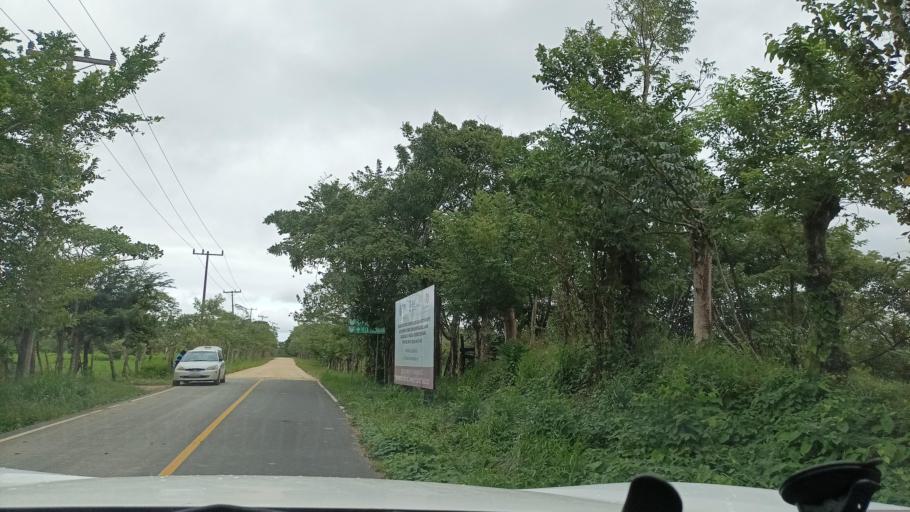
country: MX
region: Veracruz
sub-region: Moloacan
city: Cuichapa
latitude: 17.8141
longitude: -94.3553
